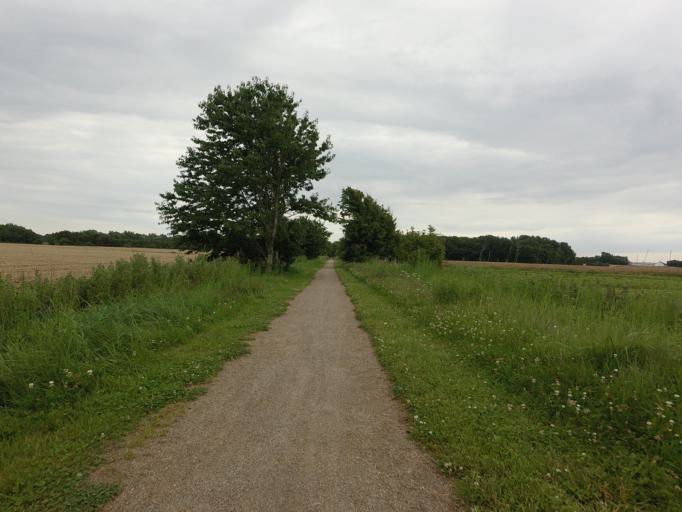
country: DK
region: North Denmark
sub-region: Alborg Kommune
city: Vadum
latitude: 57.1185
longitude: 9.8689
